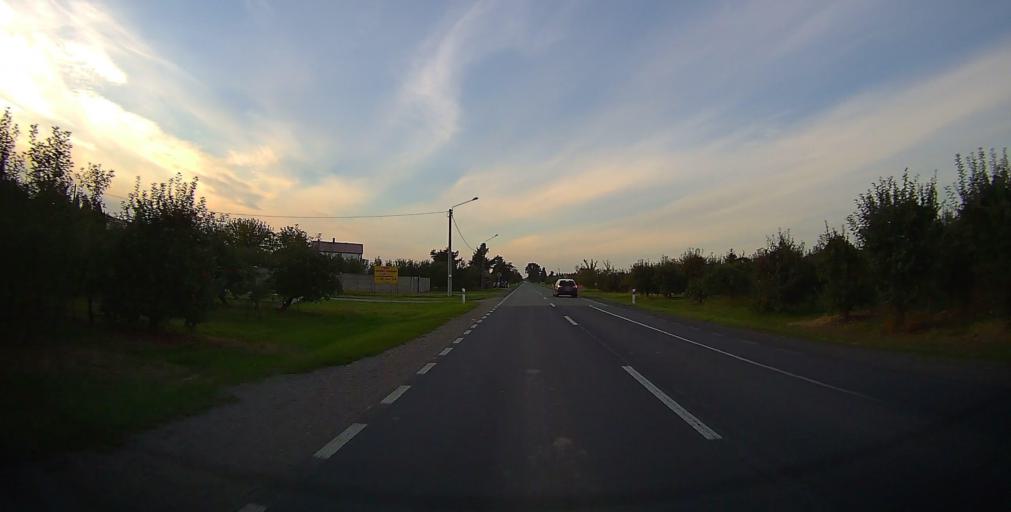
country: PL
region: Masovian Voivodeship
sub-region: Powiat garwolinski
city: Wilga
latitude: 51.8095
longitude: 21.3305
